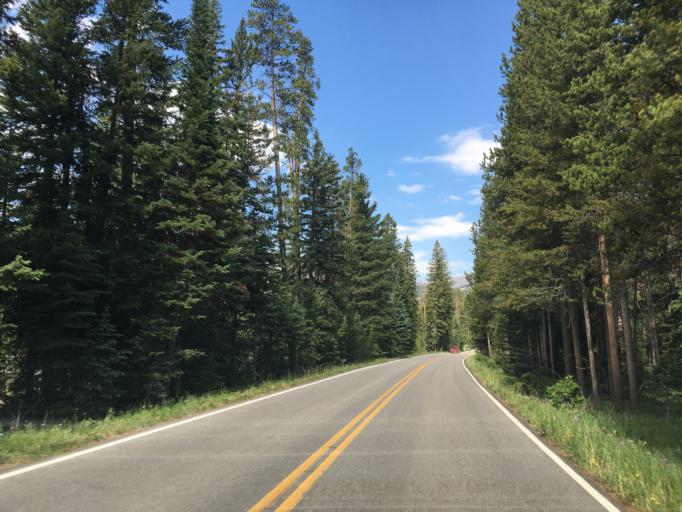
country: US
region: Montana
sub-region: Stillwater County
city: Absarokee
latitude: 45.0038
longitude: -110.0042
